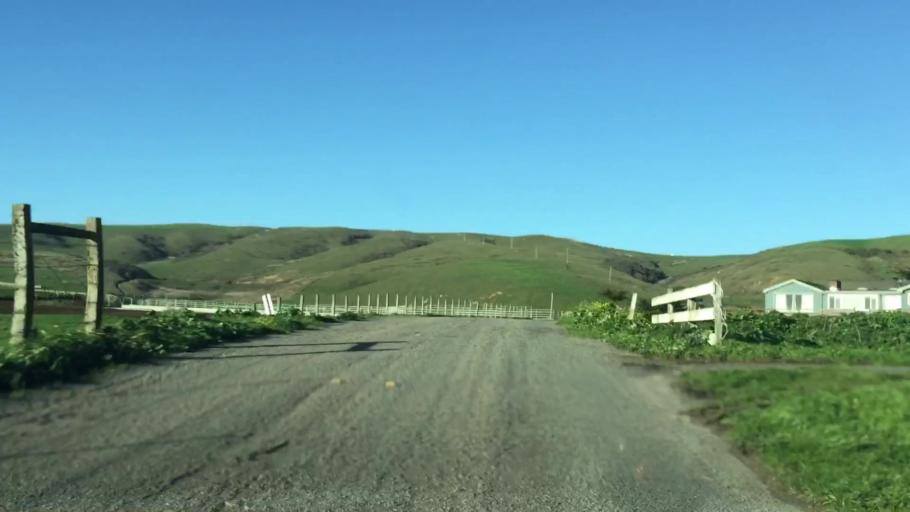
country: US
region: California
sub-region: Marin County
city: Inverness
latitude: 38.1589
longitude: -122.9382
